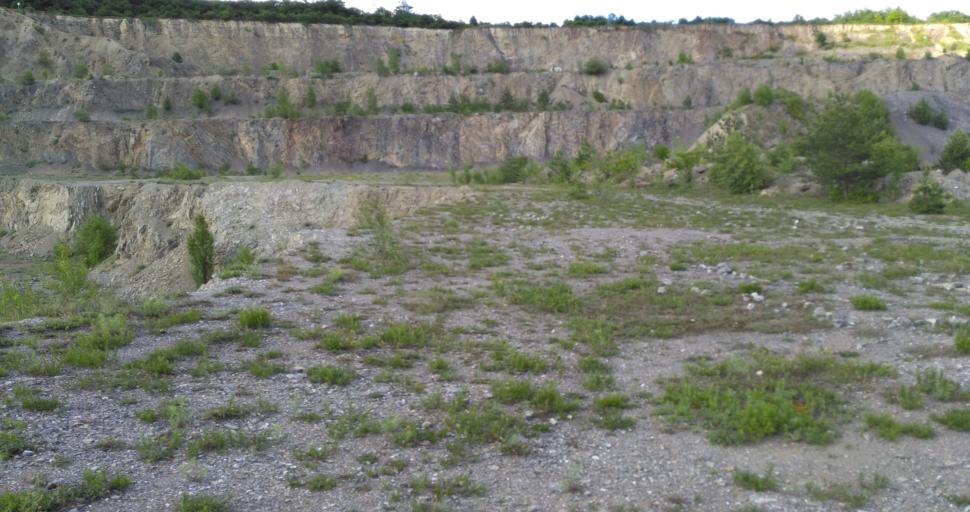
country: CZ
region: South Moravian
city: Bilovice nad Svitavou
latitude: 49.2177
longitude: 16.6704
